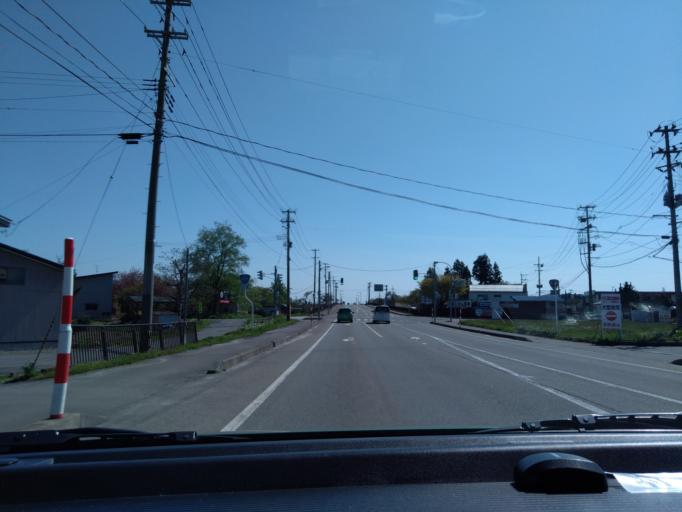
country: JP
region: Akita
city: Kakunodatemachi
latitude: 39.5834
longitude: 140.5697
